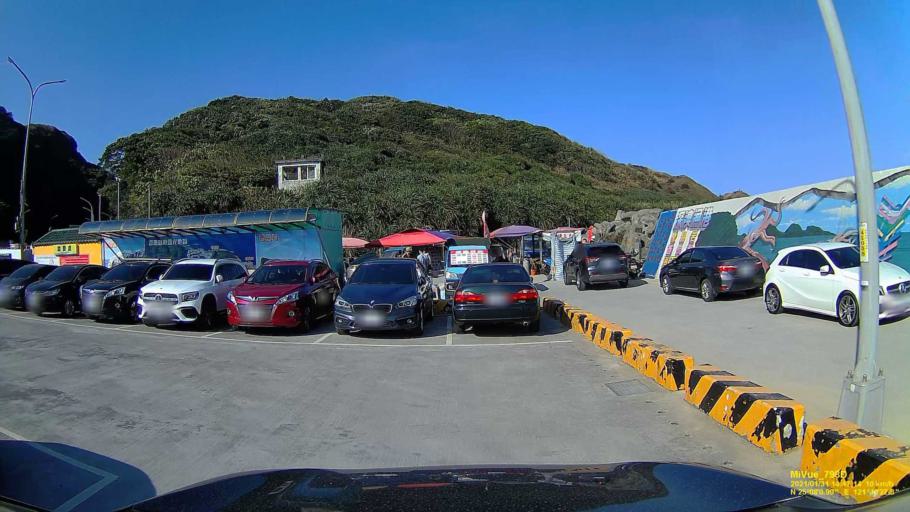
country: TW
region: Taiwan
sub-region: Keelung
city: Keelung
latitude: 25.1336
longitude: 121.8230
